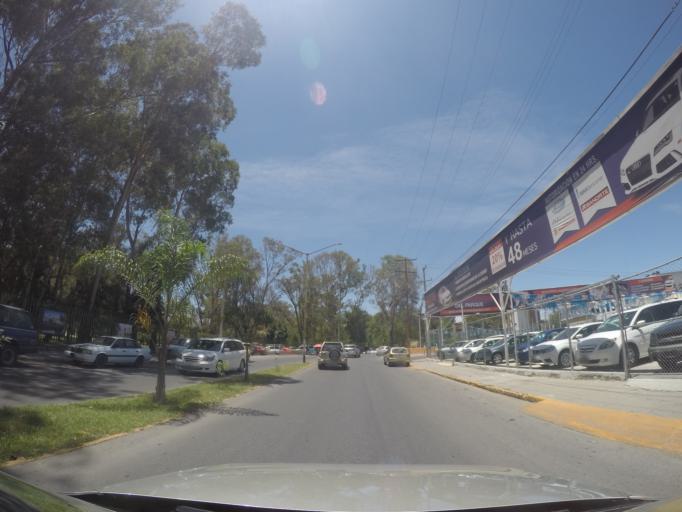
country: MX
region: San Luis Potosi
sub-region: San Luis Potosi
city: San Luis Potosi
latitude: 22.1501
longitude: -101.0151
